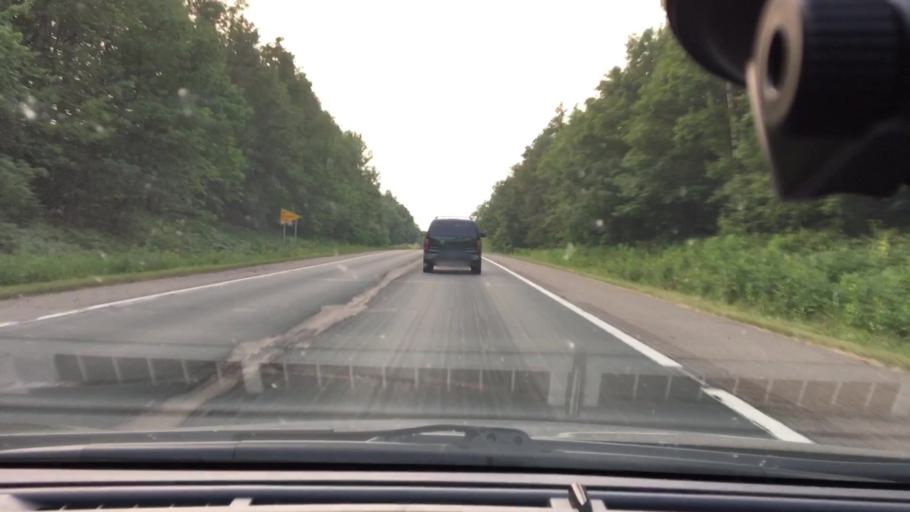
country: US
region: Minnesota
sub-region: Mille Lacs County
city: Vineland
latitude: 46.2401
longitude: -93.8042
